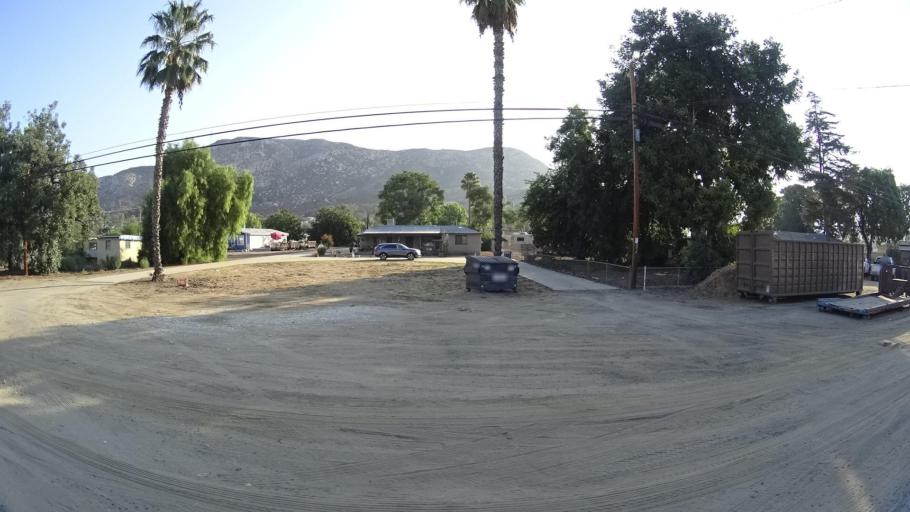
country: US
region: California
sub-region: San Diego County
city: Lakeside
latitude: 32.8798
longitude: -116.9224
